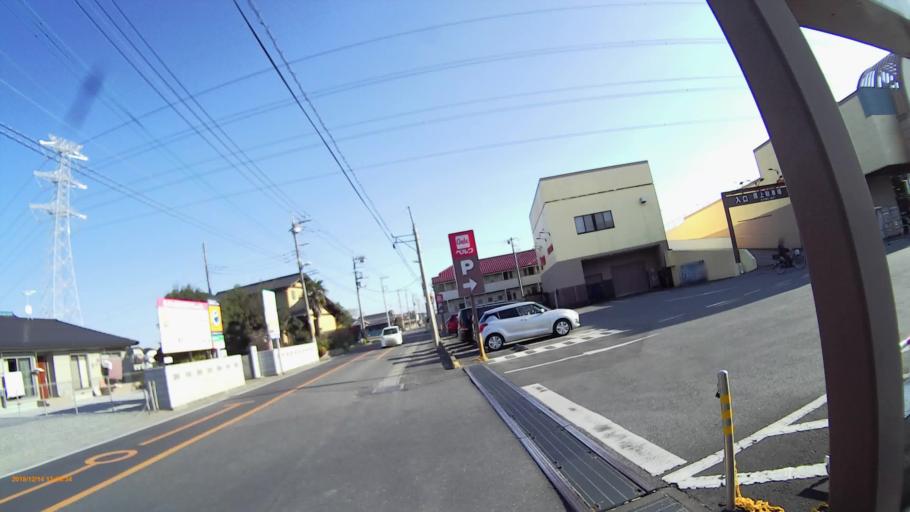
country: JP
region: Saitama
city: Konosu
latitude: 36.0748
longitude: 139.4880
